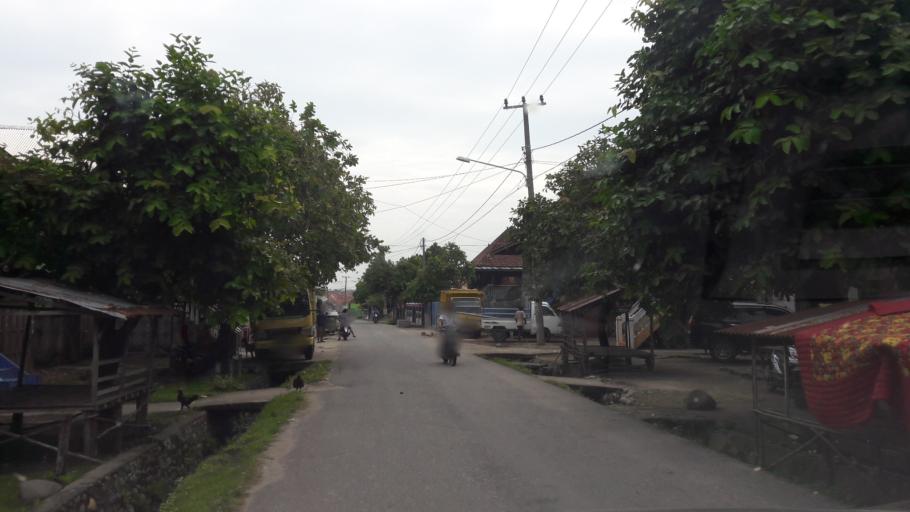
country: ID
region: South Sumatra
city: Gunungmenang
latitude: -3.1100
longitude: 104.0802
